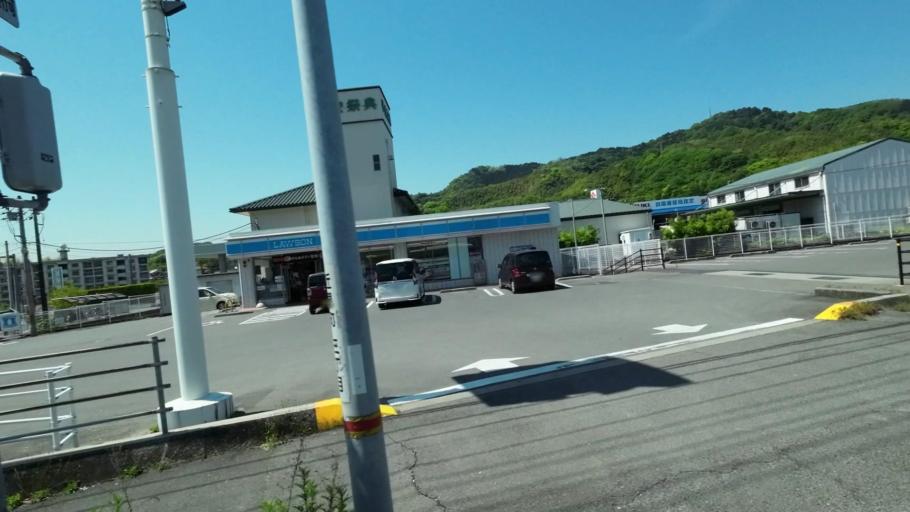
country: JP
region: Ehime
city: Hojo
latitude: 34.0902
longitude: 132.9831
